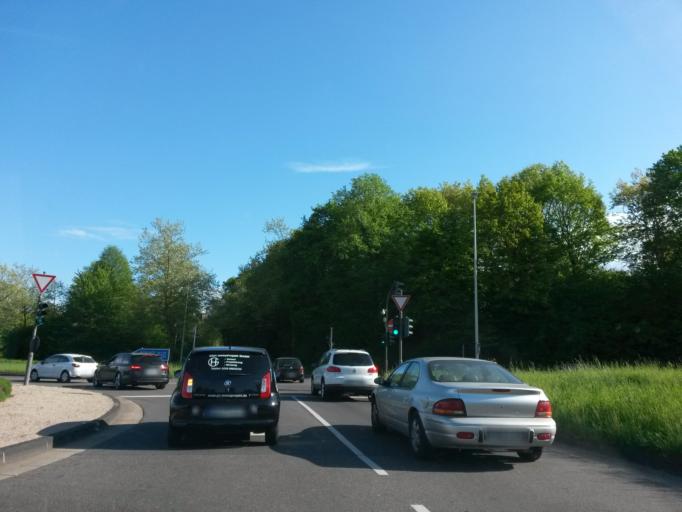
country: DE
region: North Rhine-Westphalia
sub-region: Regierungsbezirk Koln
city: Bonn
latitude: 50.7039
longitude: 7.0584
